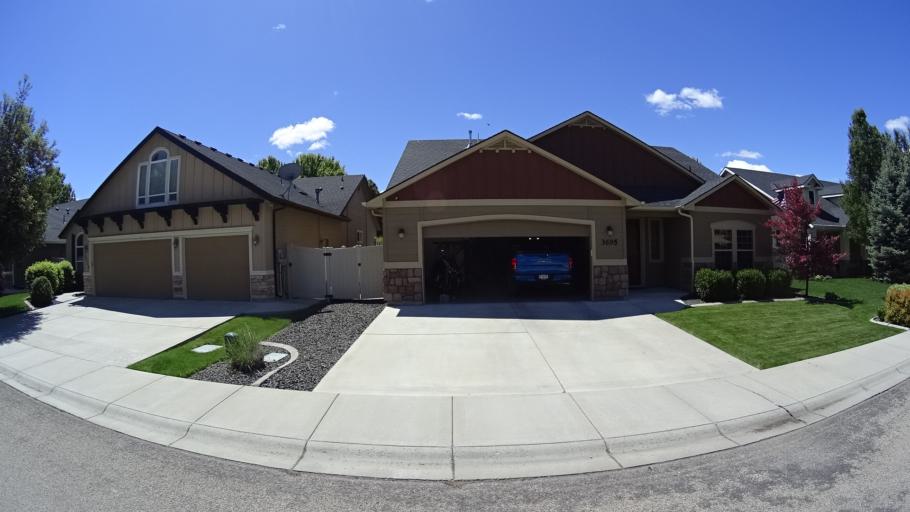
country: US
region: Idaho
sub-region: Ada County
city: Meridian
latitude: 43.6282
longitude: -116.3485
